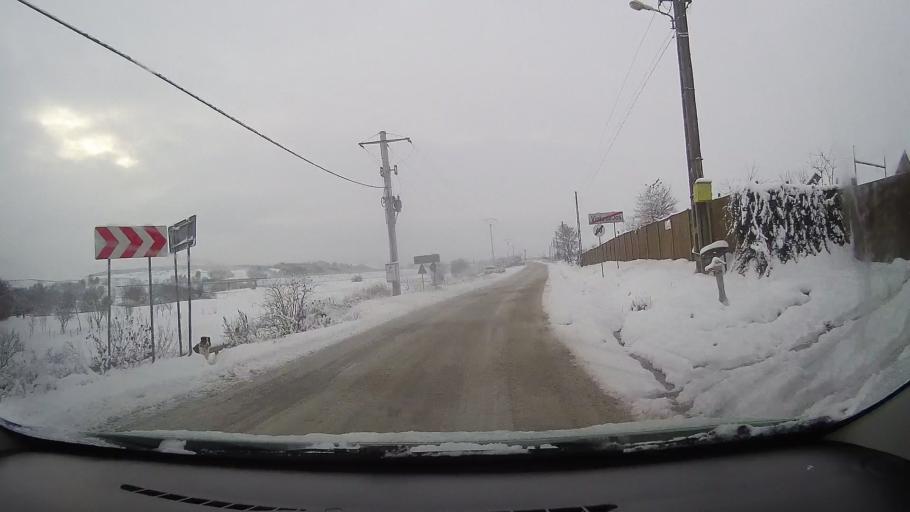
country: RO
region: Alba
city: Vurpar
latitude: 45.9733
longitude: 23.4809
